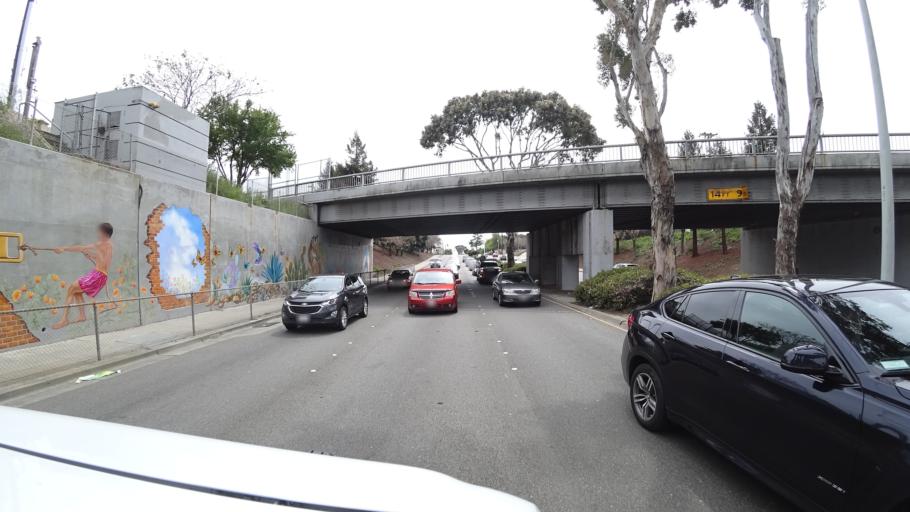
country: US
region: California
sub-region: Alameda County
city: Hayward
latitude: 37.6560
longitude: -122.0877
